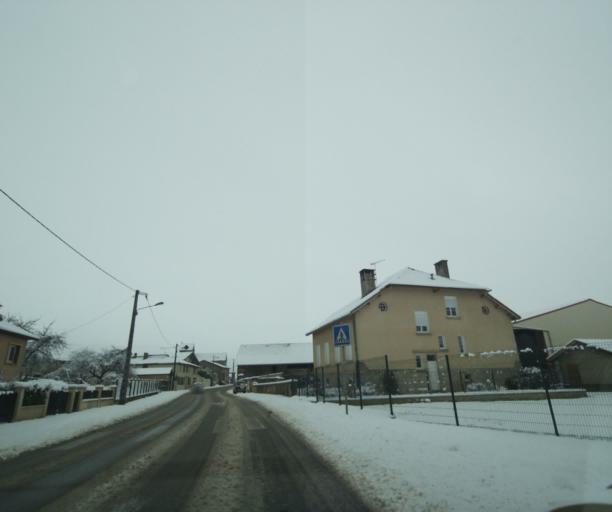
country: FR
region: Champagne-Ardenne
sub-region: Departement de la Haute-Marne
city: Wassy
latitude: 48.5265
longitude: 4.9287
